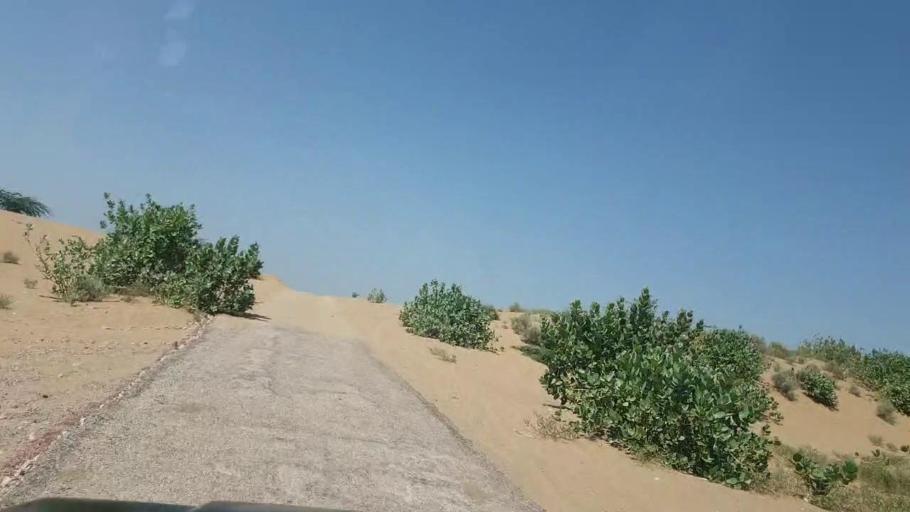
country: PK
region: Sindh
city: Chor
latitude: 25.3530
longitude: 70.3417
